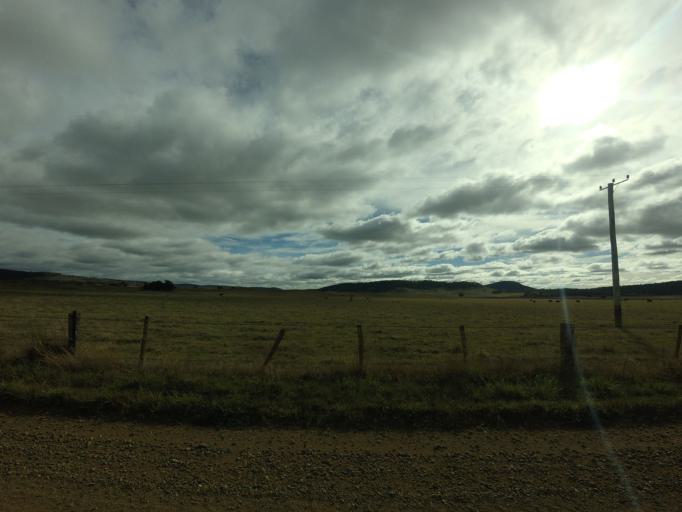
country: AU
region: Tasmania
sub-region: Brighton
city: Bridgewater
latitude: -42.4216
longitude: 147.3917
